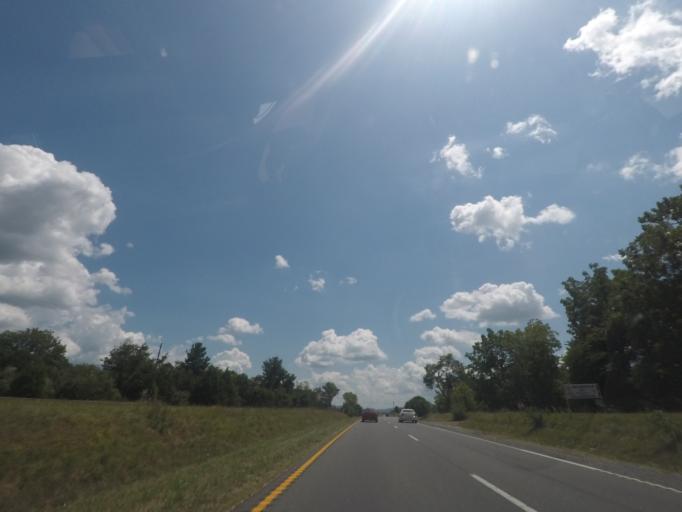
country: US
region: Virginia
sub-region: City of Winchester
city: Winchester
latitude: 39.0936
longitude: -78.1014
